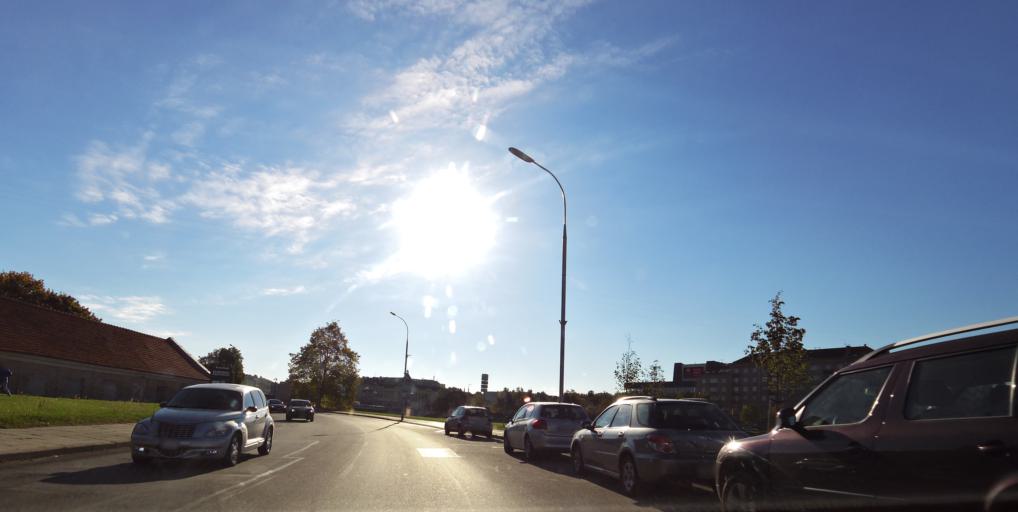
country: LT
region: Vilnius County
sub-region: Vilnius
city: Vilnius
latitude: 54.6926
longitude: 25.2769
